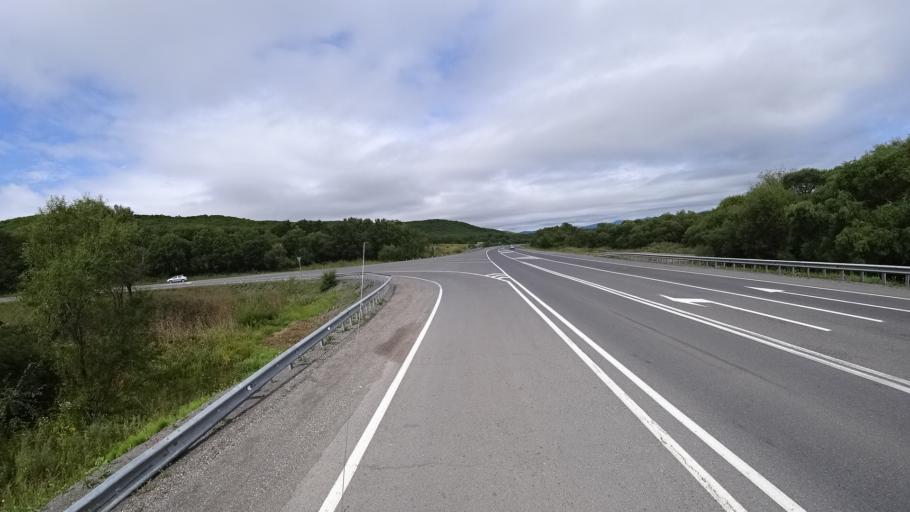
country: RU
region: Primorskiy
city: Lyalichi
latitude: 44.1387
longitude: 132.4288
